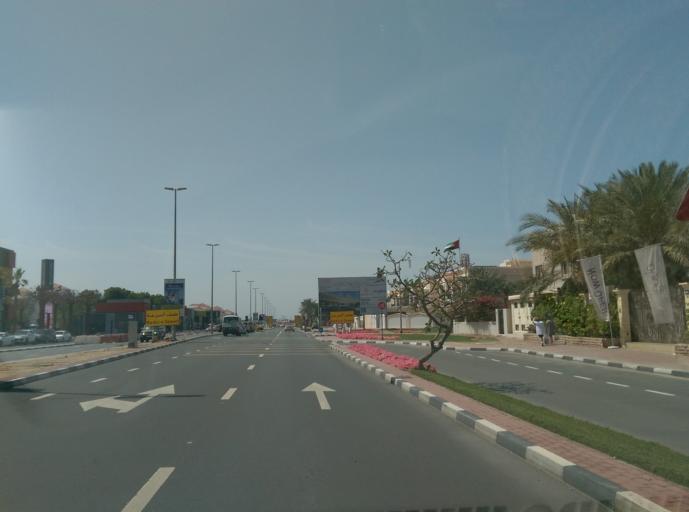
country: AE
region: Dubai
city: Dubai
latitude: 25.1994
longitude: 55.2484
